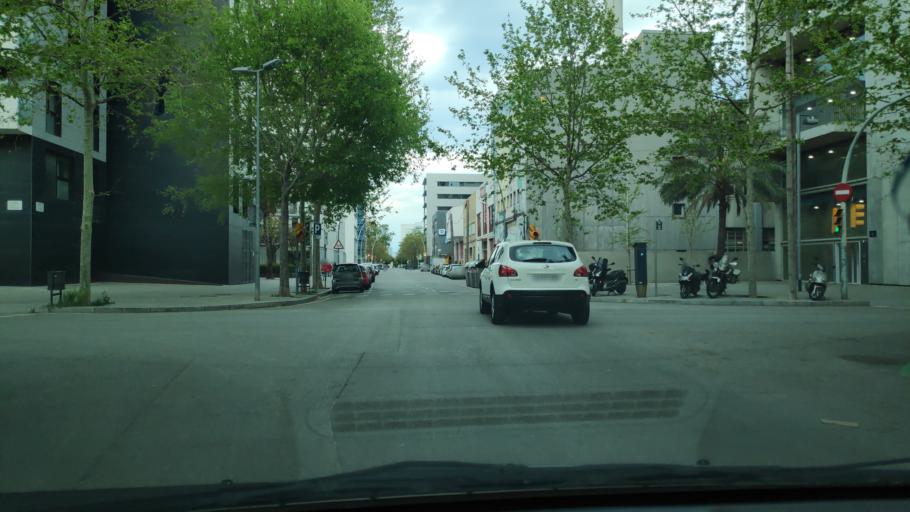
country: ES
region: Catalonia
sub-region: Provincia de Barcelona
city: Sant Marti
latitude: 41.4076
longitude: 2.2062
